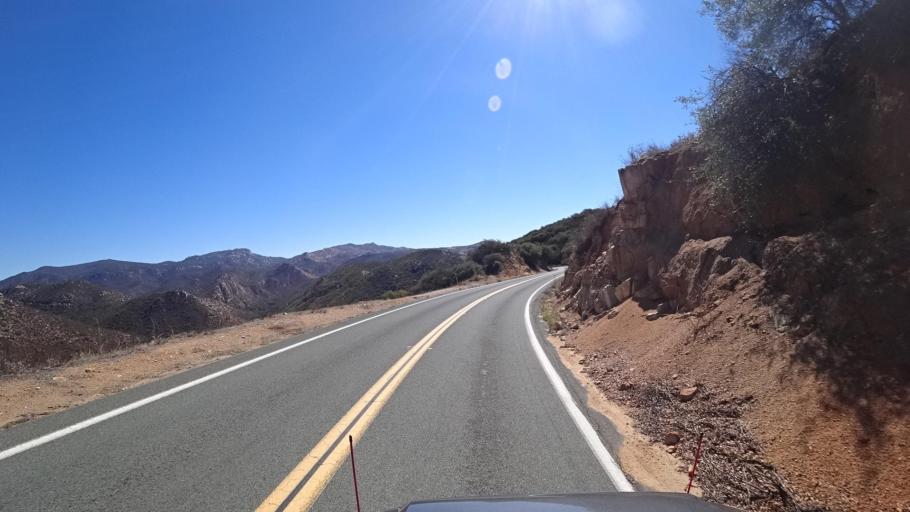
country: US
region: California
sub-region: San Diego County
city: Descanso
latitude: 32.7538
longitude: -116.6734
